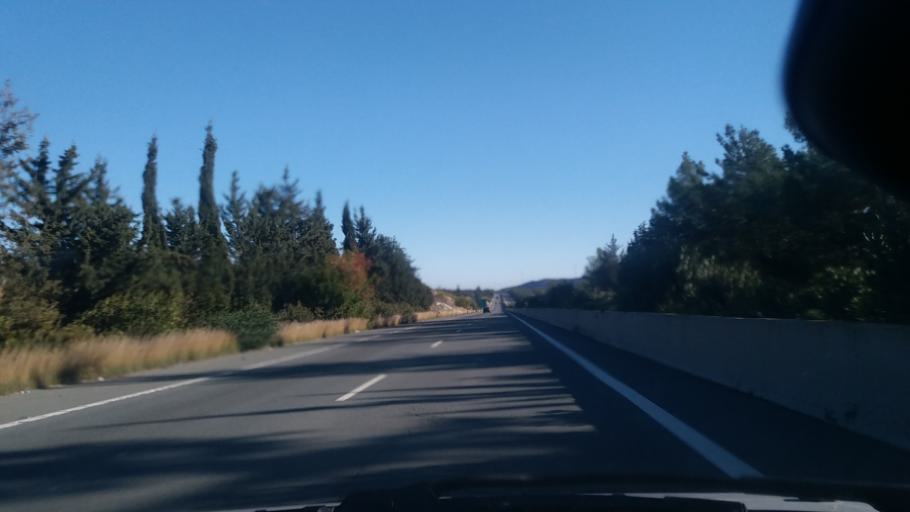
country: CY
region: Larnaka
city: Tersefanou
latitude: 34.8630
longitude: 33.4785
